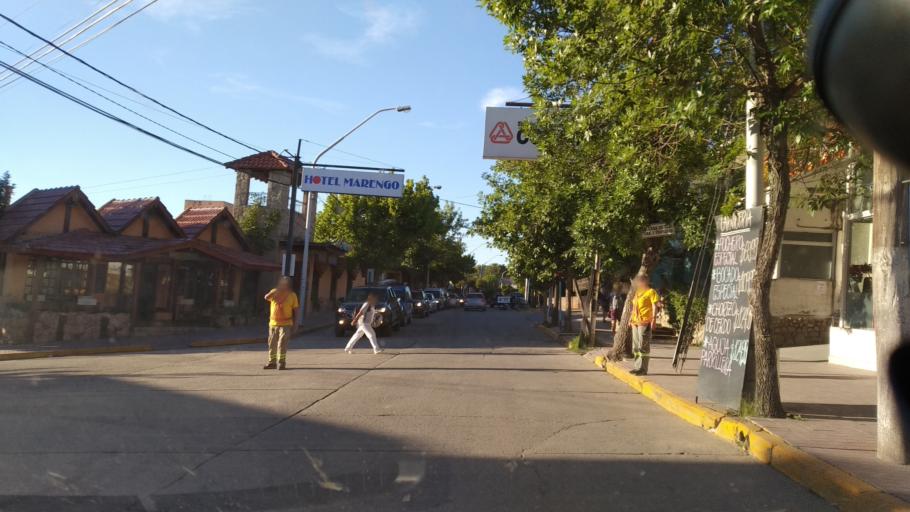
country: AR
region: Cordoba
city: Mina Clavero
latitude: -31.7189
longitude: -65.0052
